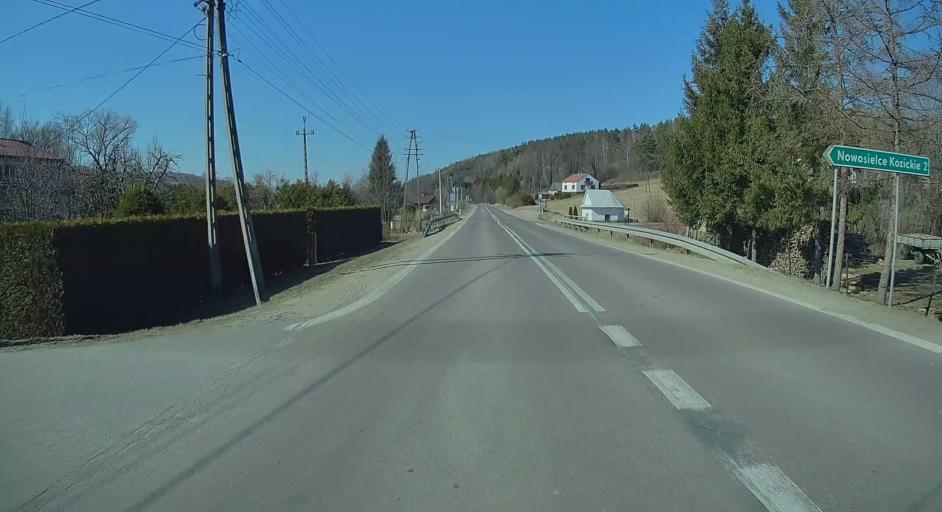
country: PL
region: Subcarpathian Voivodeship
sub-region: Powiat przemyski
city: Bircza
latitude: 49.5725
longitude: 22.5527
